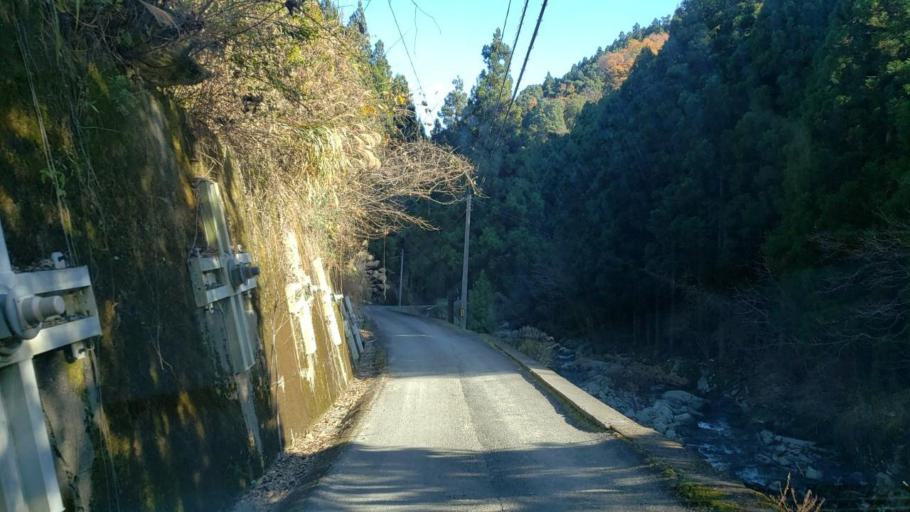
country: JP
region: Tokushima
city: Wakimachi
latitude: 33.9895
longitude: 133.9880
